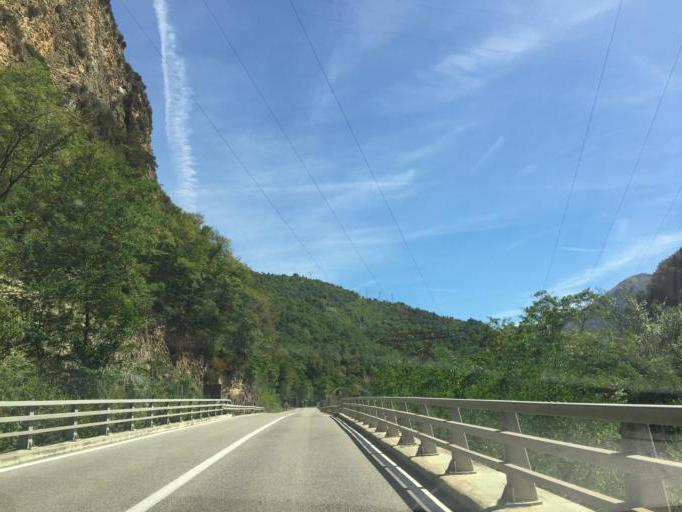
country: FR
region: Provence-Alpes-Cote d'Azur
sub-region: Departement des Alpes-Maritimes
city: Saint-Martin-Vesubie
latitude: 44.0057
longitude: 7.1368
